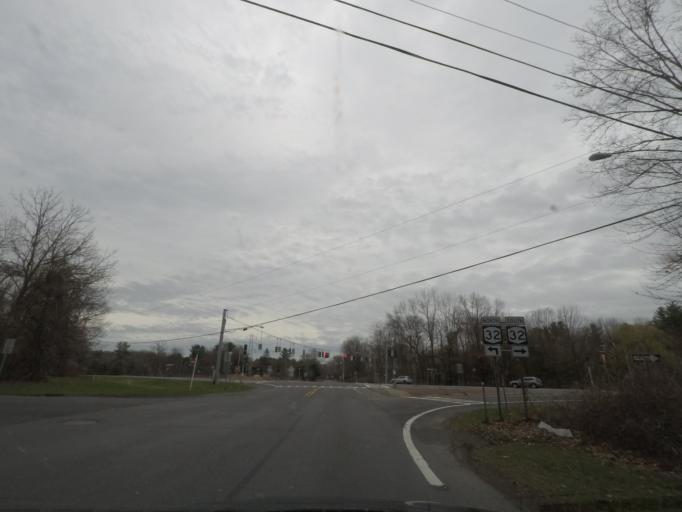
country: US
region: New York
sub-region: Albany County
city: Delmar
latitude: 42.6060
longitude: -73.8351
